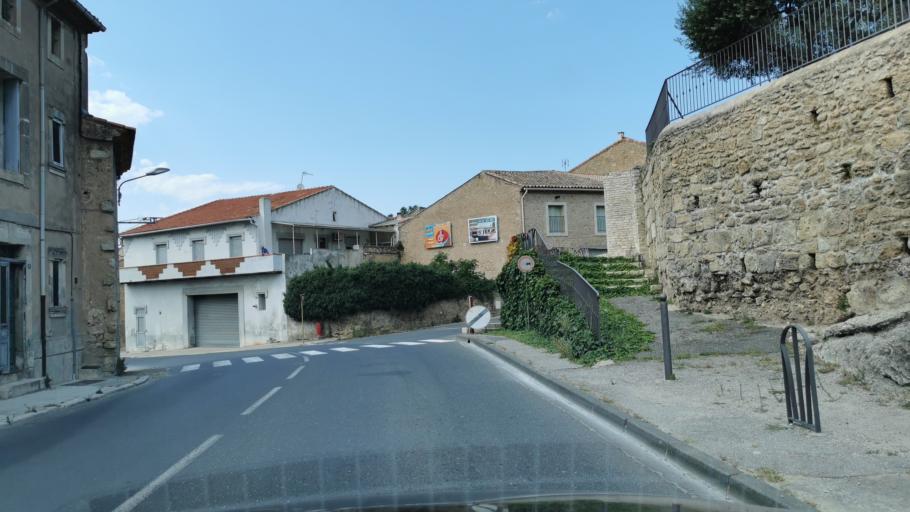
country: FR
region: Languedoc-Roussillon
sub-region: Departement de l'Herault
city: Puisserguier
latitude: 43.3682
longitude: 3.0435
